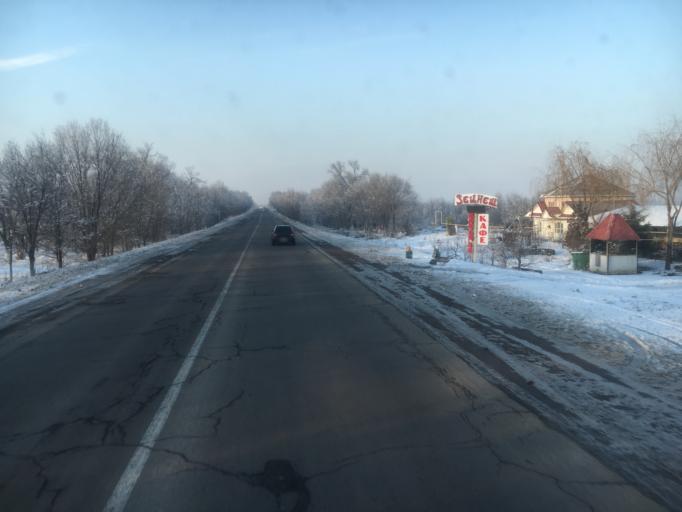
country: KZ
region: Almaty Oblysy
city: Burunday
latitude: 43.3112
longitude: 76.6660
